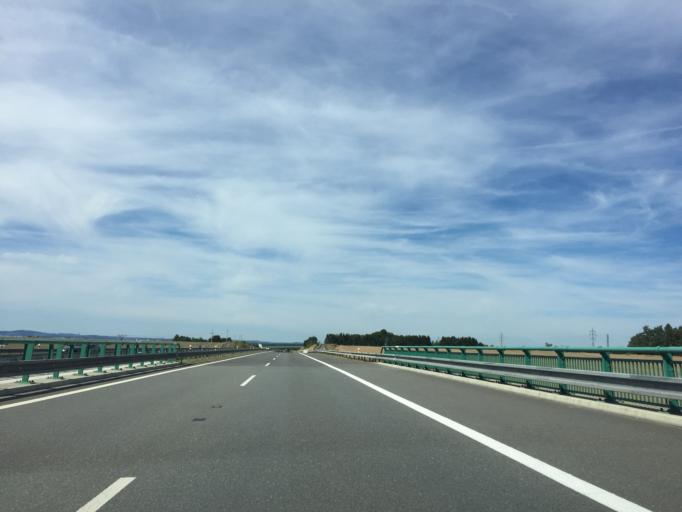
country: CZ
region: Jihocesky
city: Plana nad Luznici
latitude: 49.3148
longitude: 14.7389
